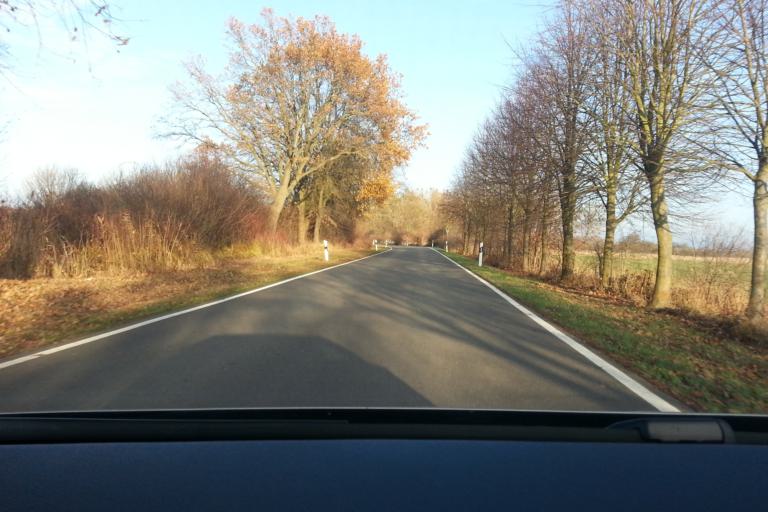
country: DE
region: Mecklenburg-Vorpommern
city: Ducherow
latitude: 53.6605
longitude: 13.7109
